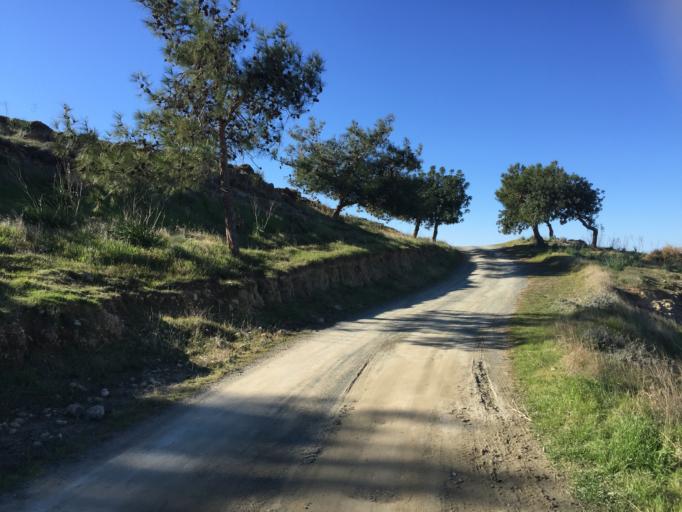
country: CY
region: Limassol
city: Pissouri
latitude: 34.6681
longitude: 32.6928
